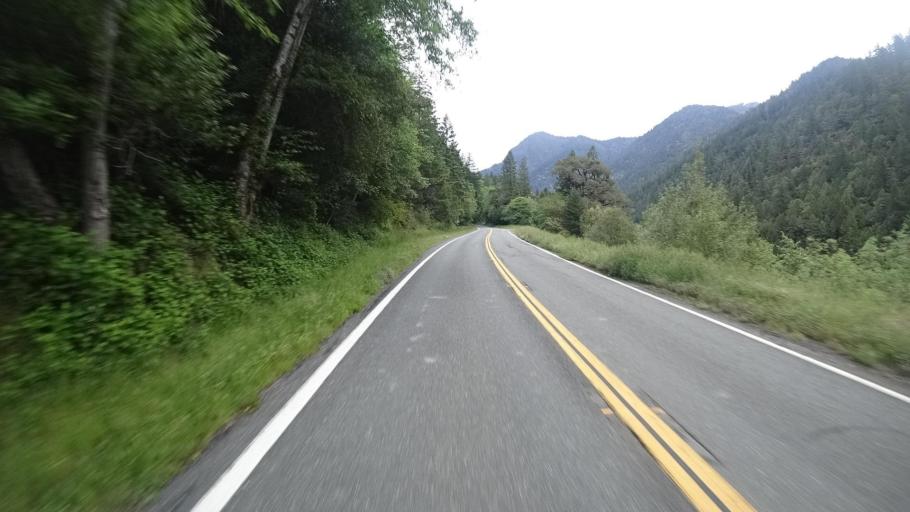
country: US
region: California
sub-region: Humboldt County
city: Willow Creek
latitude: 41.2054
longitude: -123.6627
